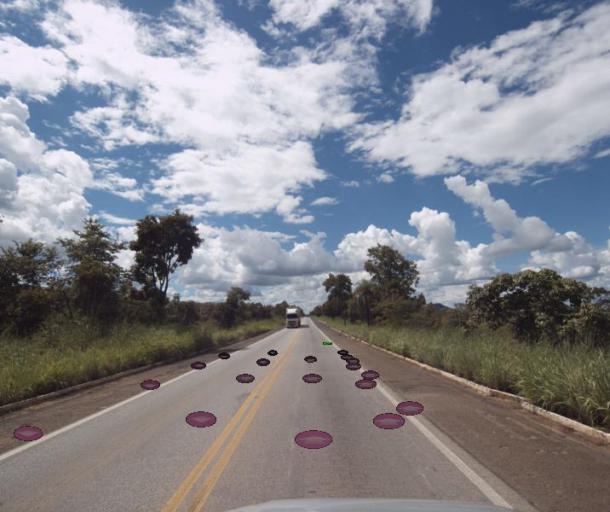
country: BR
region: Goias
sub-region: Porangatu
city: Porangatu
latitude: -13.8634
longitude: -49.0508
